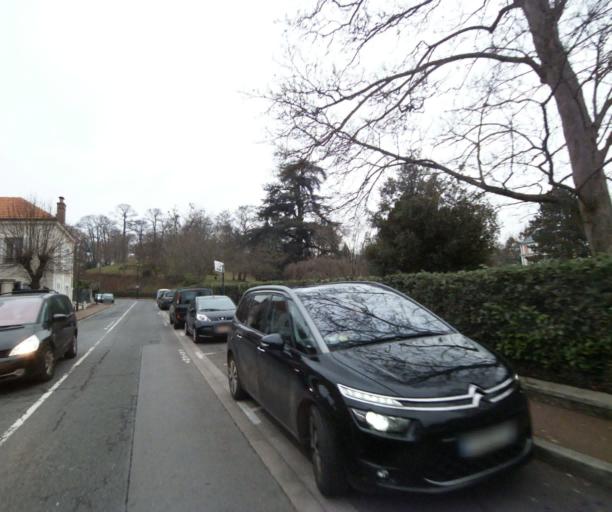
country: FR
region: Ile-de-France
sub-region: Departement des Hauts-de-Seine
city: Vaucresson
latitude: 48.8397
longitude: 2.1584
